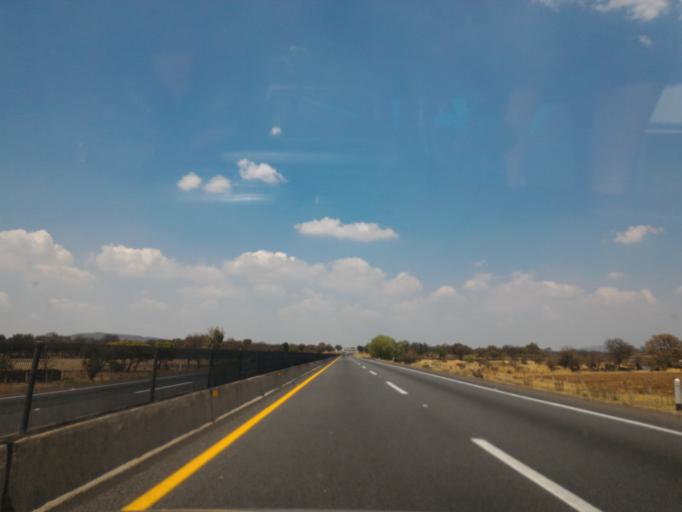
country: MX
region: Jalisco
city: Tepatitlan de Morelos
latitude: 20.8622
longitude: -102.7625
